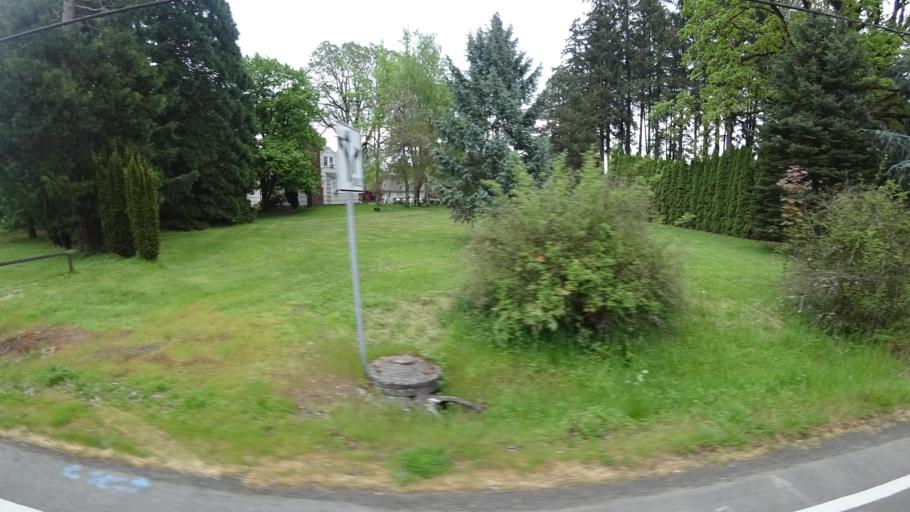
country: US
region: Oregon
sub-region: Washington County
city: Hillsboro
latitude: 45.5492
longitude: -122.9797
